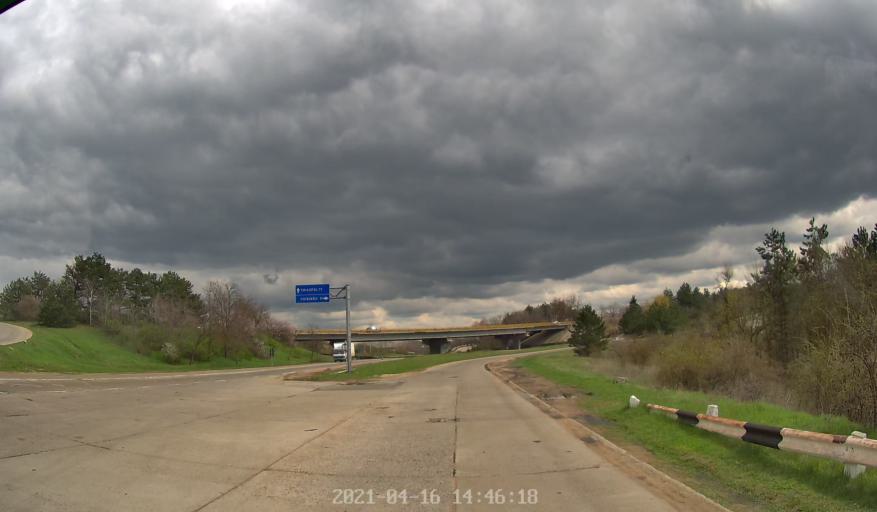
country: MD
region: Chisinau
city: Stauceni
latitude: 47.1114
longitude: 28.8601
